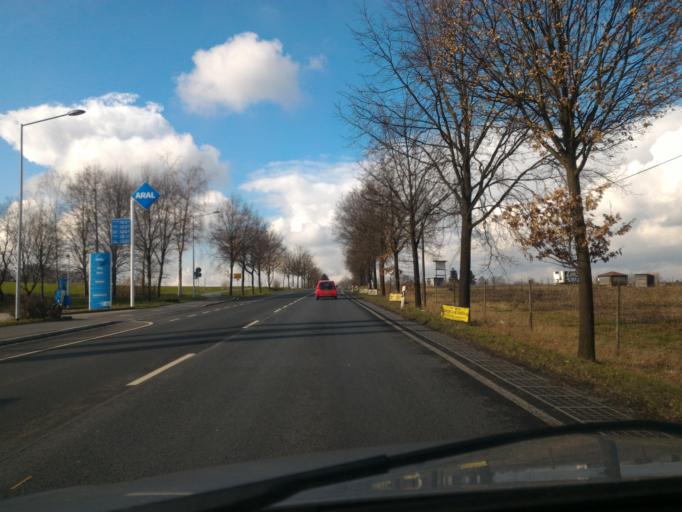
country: DE
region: Saxony
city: Radeberg
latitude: 51.0606
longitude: 13.8747
